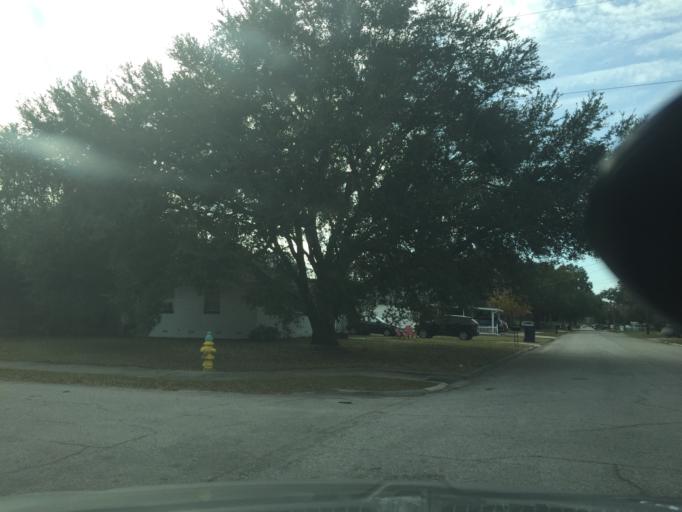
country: US
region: Florida
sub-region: Hillsborough County
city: Tampa
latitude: 27.9472
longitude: -82.4953
